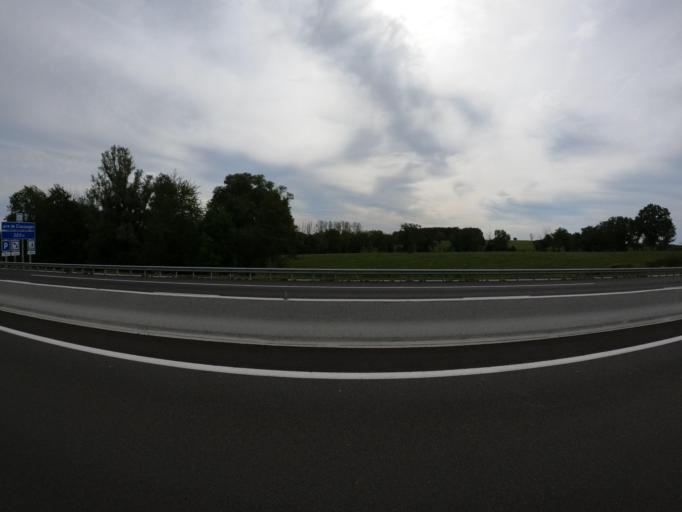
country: FR
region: Auvergne
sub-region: Departement de l'Allier
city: Souvigny
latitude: 46.4412
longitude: 3.1500
